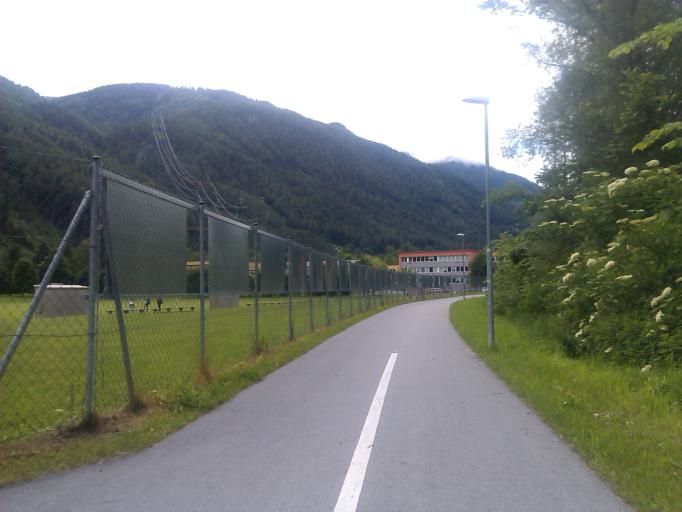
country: AT
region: Tyrol
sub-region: Politischer Bezirk Landeck
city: Fendels
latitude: 47.0661
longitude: 10.6610
